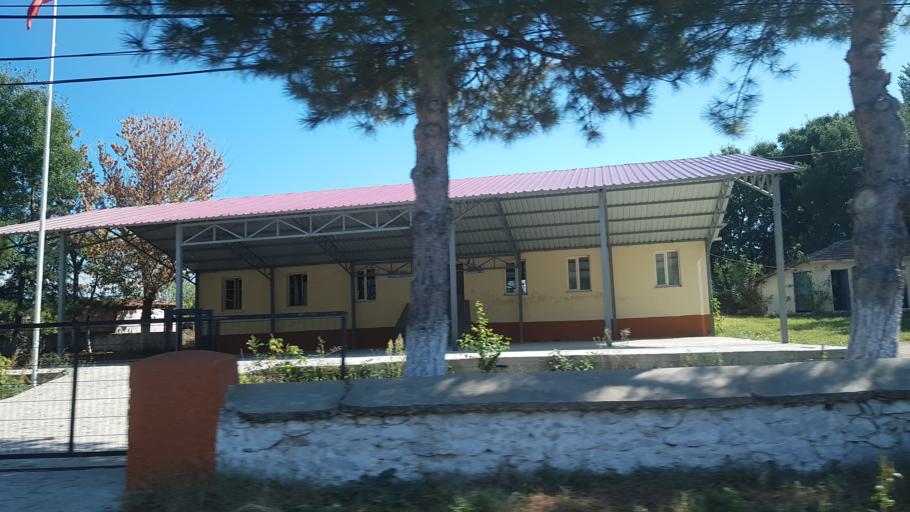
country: TR
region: Kirklareli
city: Kirklareli
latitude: 41.7754
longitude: 27.2269
